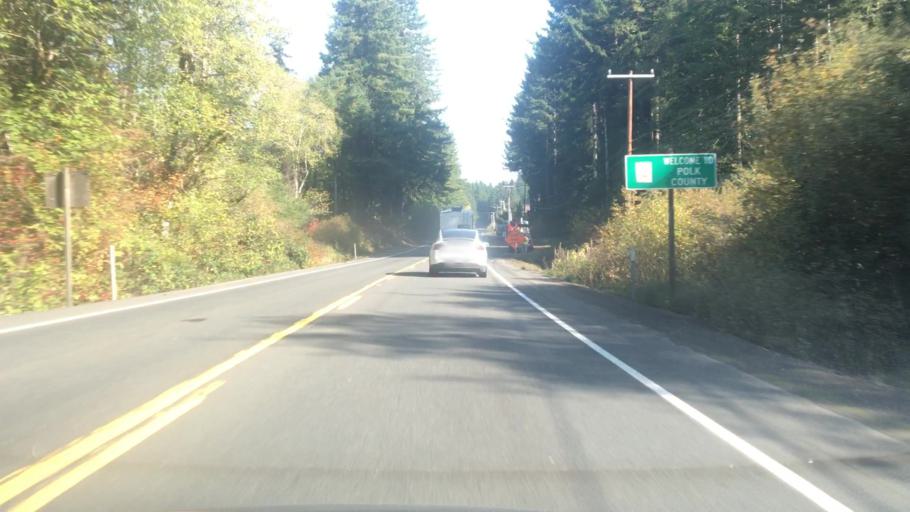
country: US
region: Oregon
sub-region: Polk County
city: Grand Ronde
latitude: 45.0705
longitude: -123.7245
